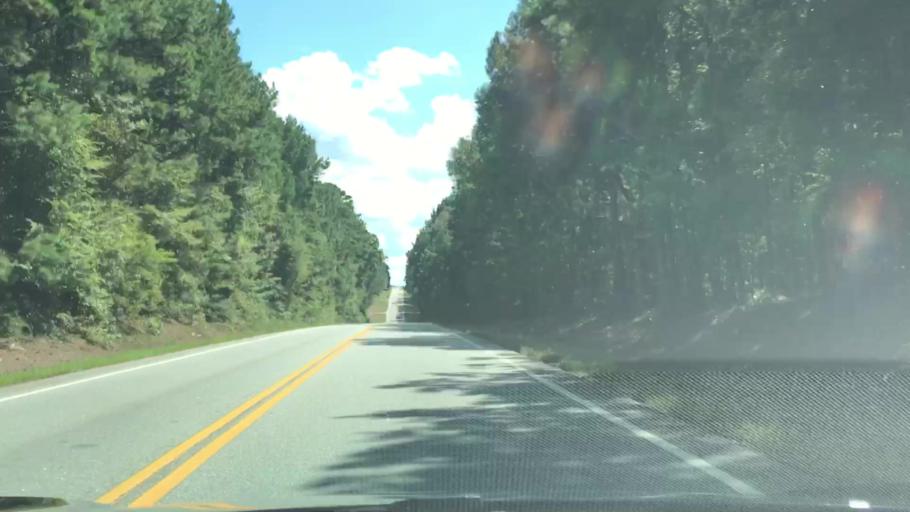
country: US
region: Georgia
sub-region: Greene County
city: Greensboro
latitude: 33.6272
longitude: -83.2145
